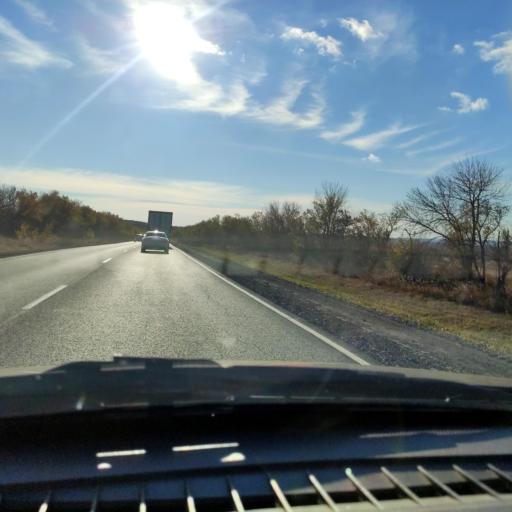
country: RU
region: Samara
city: Zhigulevsk
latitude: 53.3026
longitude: 49.3467
